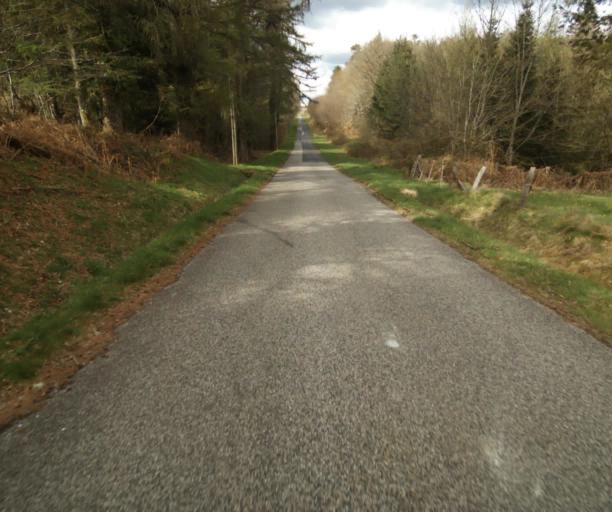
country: FR
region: Limousin
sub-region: Departement de la Correze
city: Argentat
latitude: 45.2061
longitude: 1.9662
